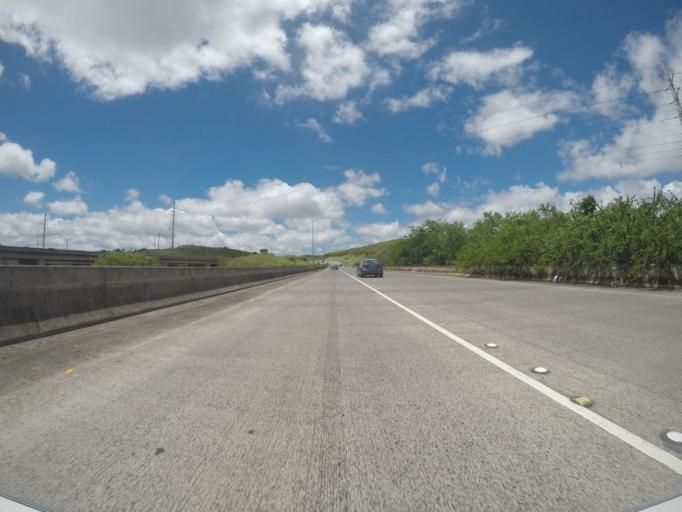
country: US
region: Hawaii
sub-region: Honolulu County
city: Pearl City, Manana
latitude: 21.4006
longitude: -157.9877
